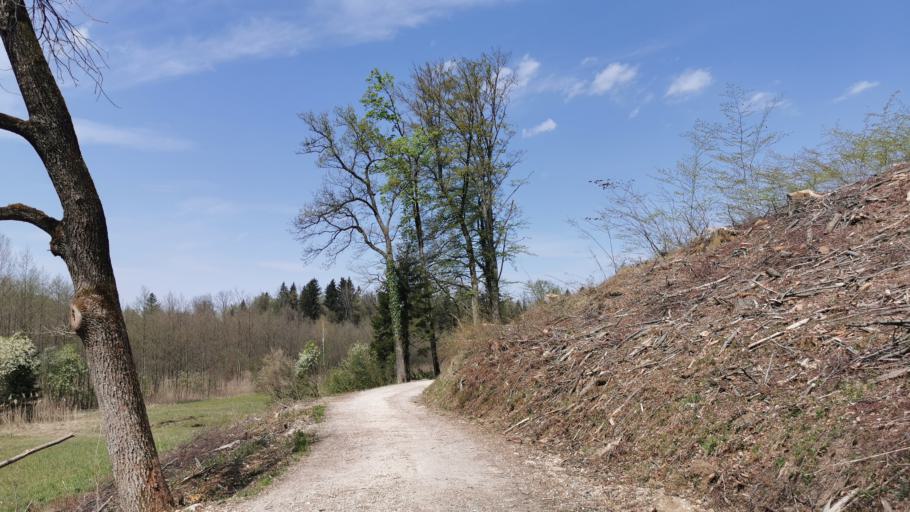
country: AT
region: Salzburg
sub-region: Politischer Bezirk Salzburg-Umgebung
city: Grodig
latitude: 47.7512
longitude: 13.0054
